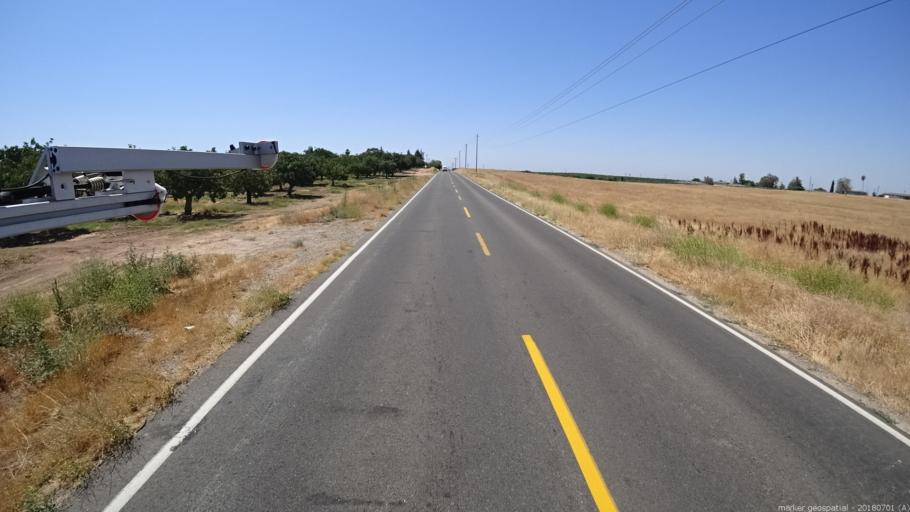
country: US
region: California
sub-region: Madera County
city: Madera Acres
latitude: 37.0362
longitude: -120.0291
